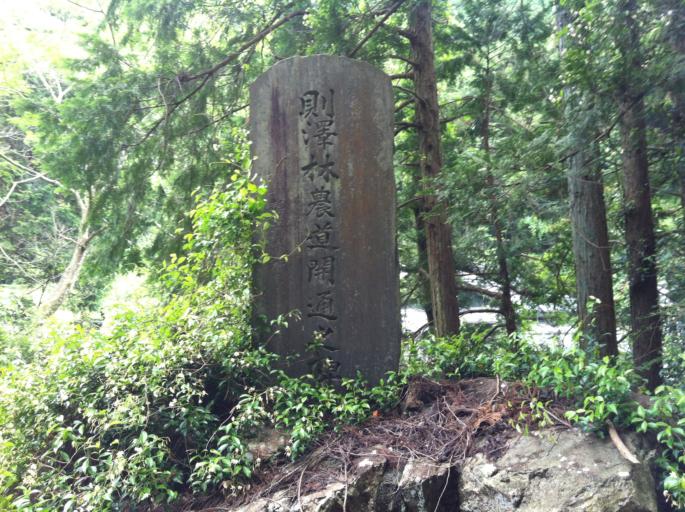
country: JP
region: Shizuoka
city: Shizuoka-shi
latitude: 35.0636
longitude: 138.4112
